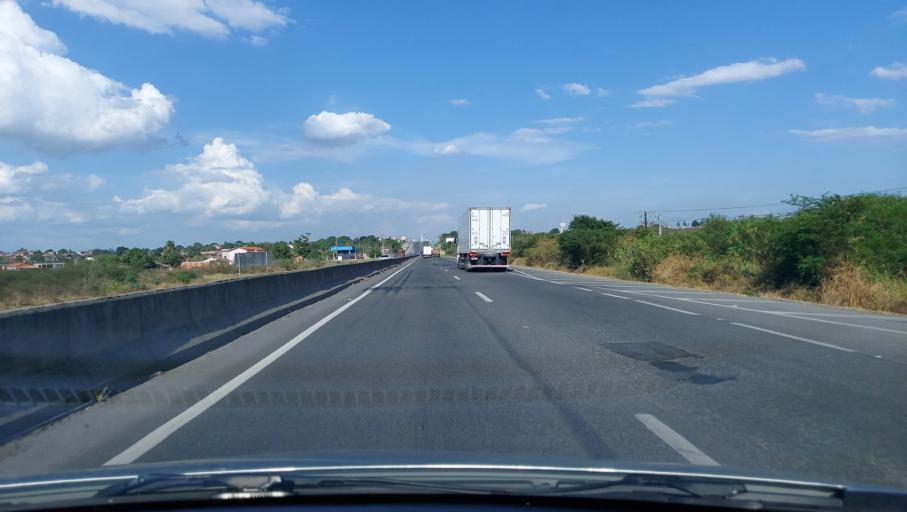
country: BR
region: Bahia
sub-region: Santo Estevao
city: Santo Estevao
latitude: -12.4535
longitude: -39.2562
